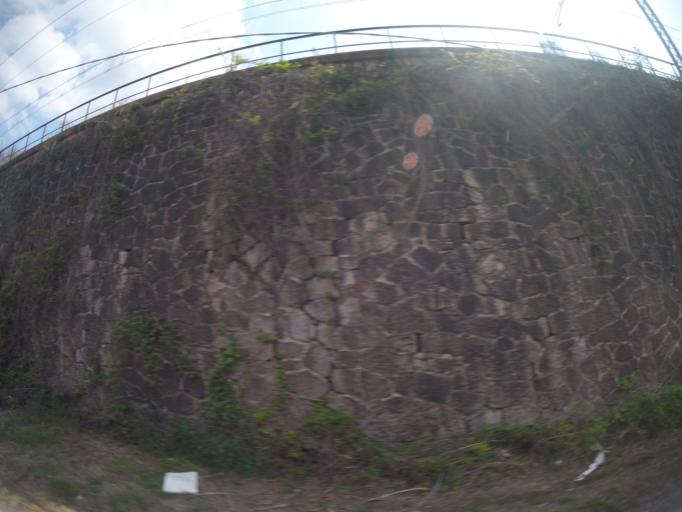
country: IT
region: Piedmont
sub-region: Provincia Verbano-Cusio-Ossola
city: Omegna
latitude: 45.8517
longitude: 8.4069
